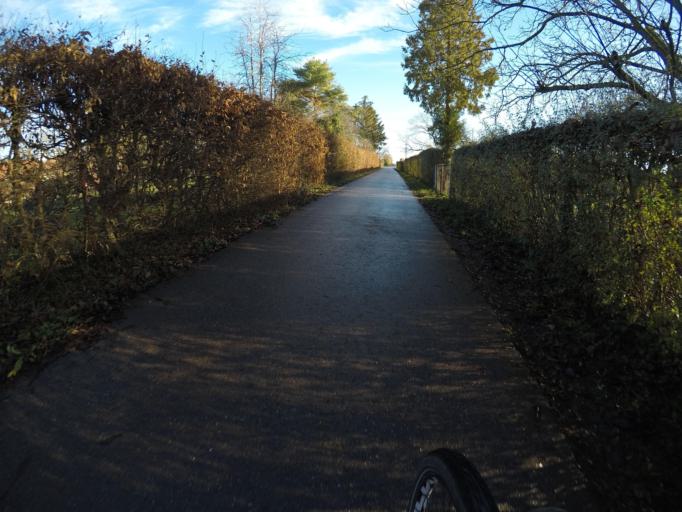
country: DE
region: Baden-Wuerttemberg
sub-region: Regierungsbezirk Stuttgart
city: Fellbach
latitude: 48.8039
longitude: 9.2567
